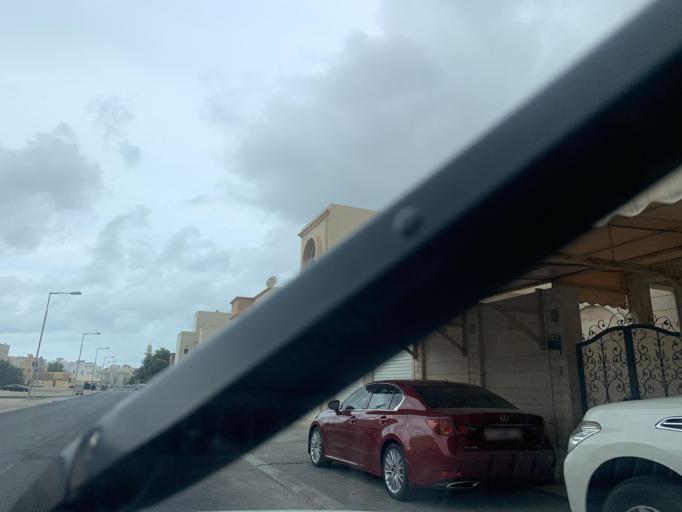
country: BH
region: Muharraq
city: Al Hadd
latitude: 26.2765
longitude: 50.6446
